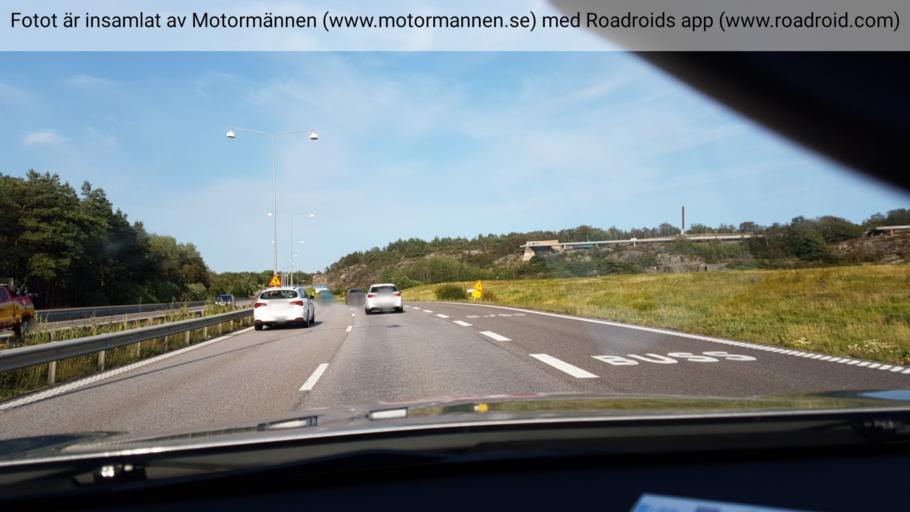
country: SE
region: Vaestra Goetaland
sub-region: Goteborg
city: Torslanda
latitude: 57.7162
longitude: 11.8042
